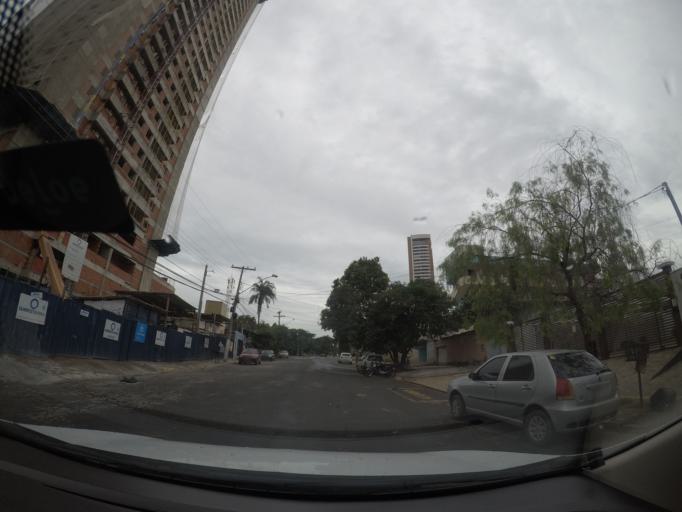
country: BR
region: Goias
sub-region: Goiania
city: Goiania
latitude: -16.6810
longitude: -49.2423
